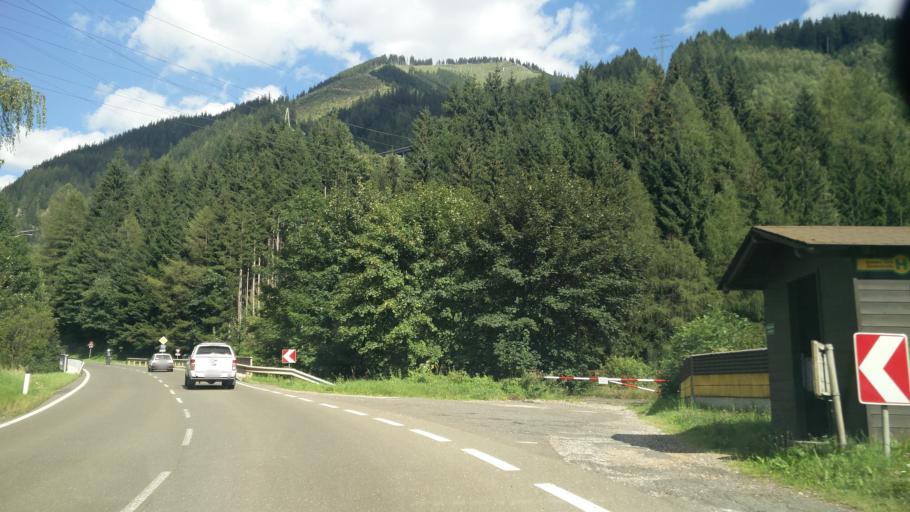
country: AT
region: Styria
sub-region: Politischer Bezirk Leoben
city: Eisenerz
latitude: 47.5406
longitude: 14.9179
